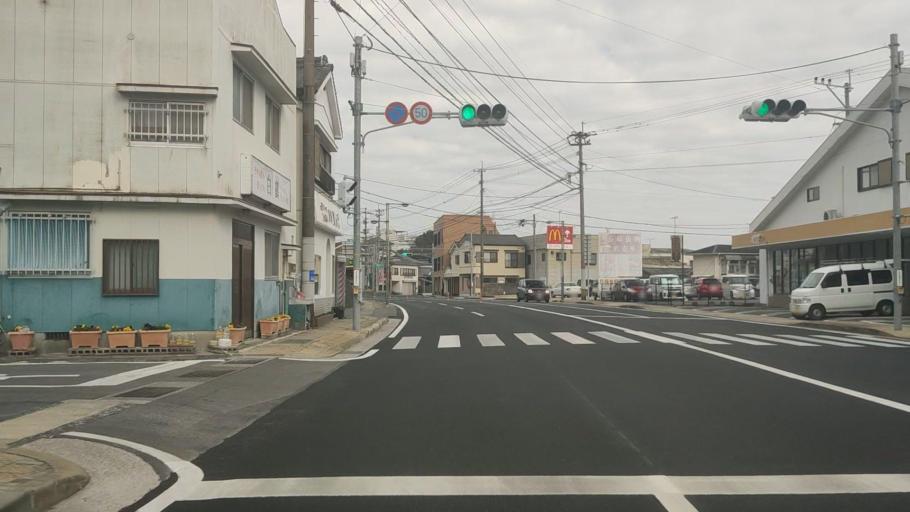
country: JP
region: Nagasaki
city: Shimabara
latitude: 32.7701
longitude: 130.3728
